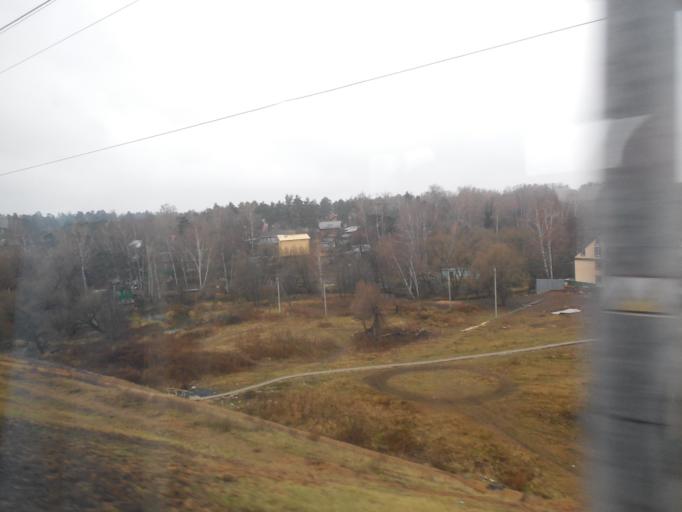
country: RU
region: Moscow
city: Zagor'ye
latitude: 55.5534
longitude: 37.6789
